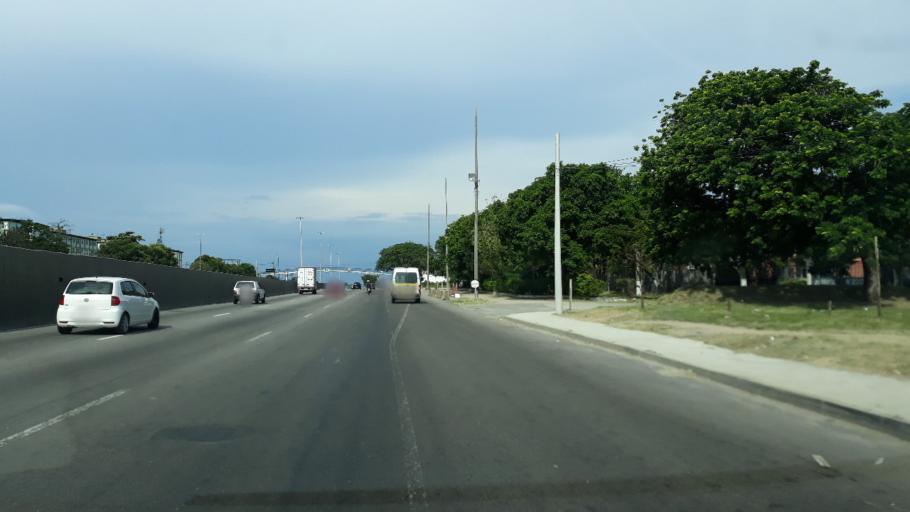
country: BR
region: Rio de Janeiro
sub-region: Sao Joao De Meriti
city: Sao Joao de Meriti
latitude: -22.8322
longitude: -43.3534
